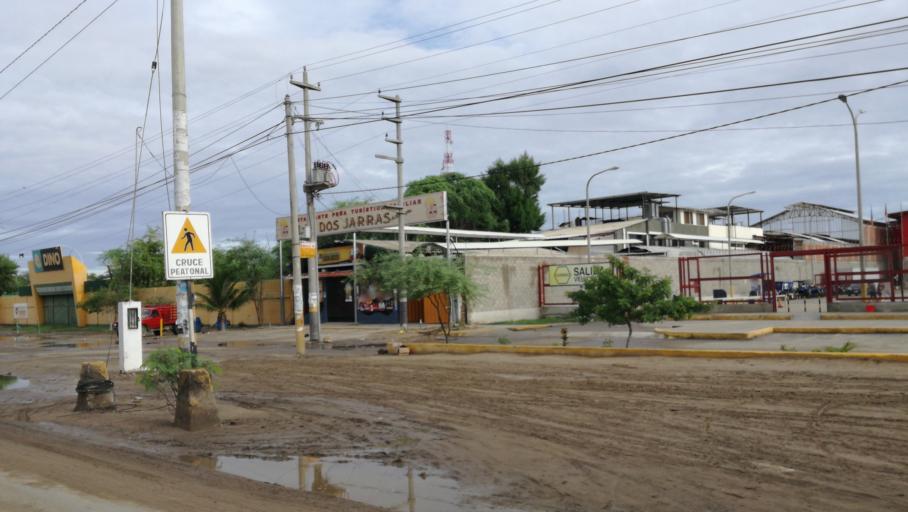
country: PE
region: Piura
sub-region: Provincia de Piura
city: Piura
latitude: -5.1825
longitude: -80.6555
